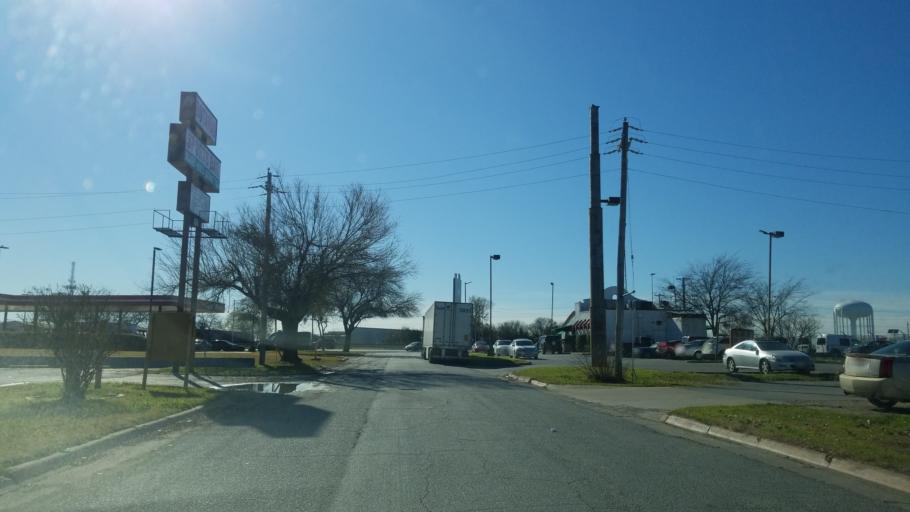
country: US
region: Texas
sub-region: Dallas County
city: Grand Prairie
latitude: 32.7414
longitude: -97.0496
